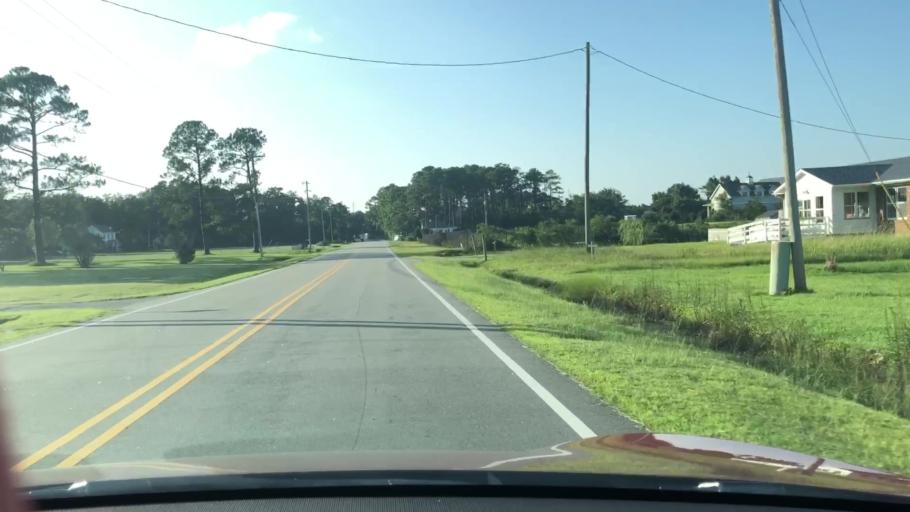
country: US
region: North Carolina
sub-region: Dare County
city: Manteo
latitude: 35.8876
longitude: -75.7639
